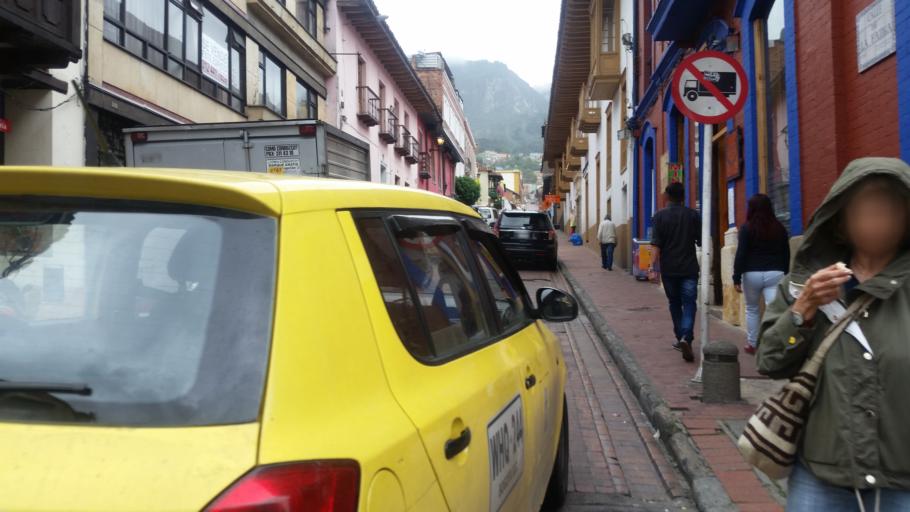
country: CO
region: Bogota D.C.
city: Bogota
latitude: 4.5957
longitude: -74.0733
